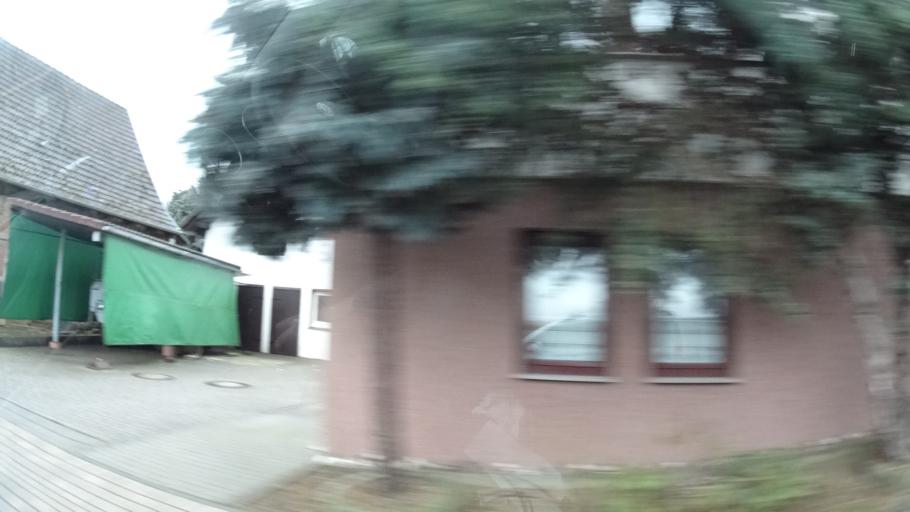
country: DE
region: Thuringia
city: Stepfershausen
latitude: 50.5964
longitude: 10.2987
